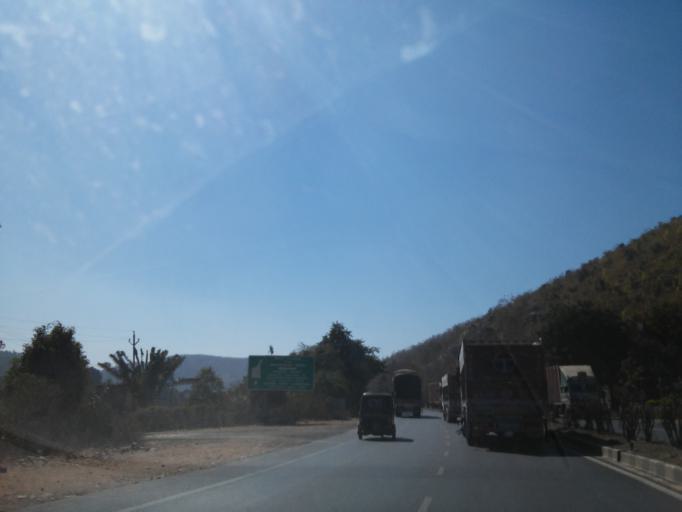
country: IN
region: Gujarat
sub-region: Sabar Kantha
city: Meghraj
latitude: 23.6966
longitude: 73.3878
